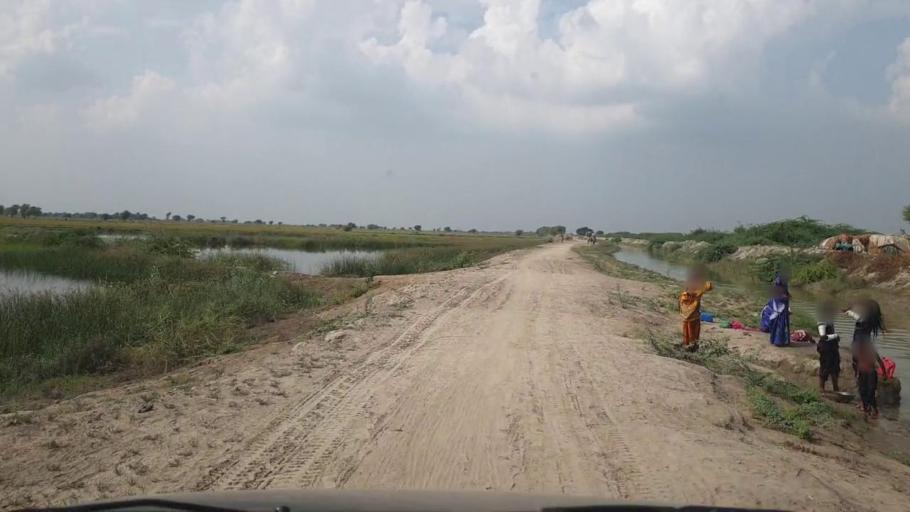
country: PK
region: Sindh
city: Badin
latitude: 24.5704
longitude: 68.6326
